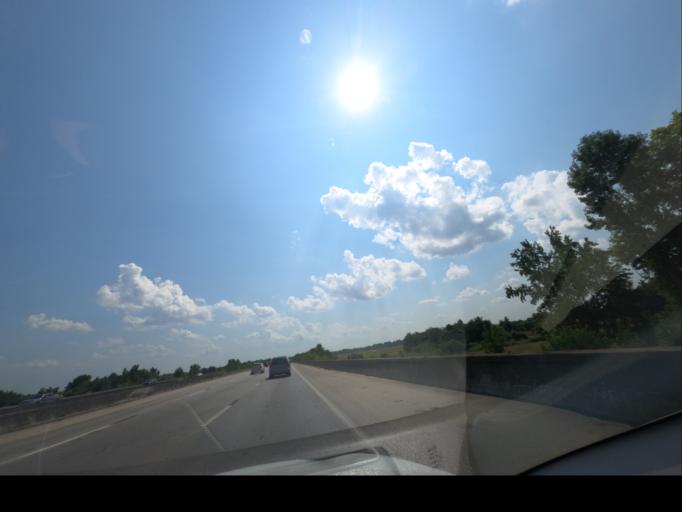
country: US
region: South Carolina
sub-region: Richland County
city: Columbia
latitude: 33.9424
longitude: -81.0033
